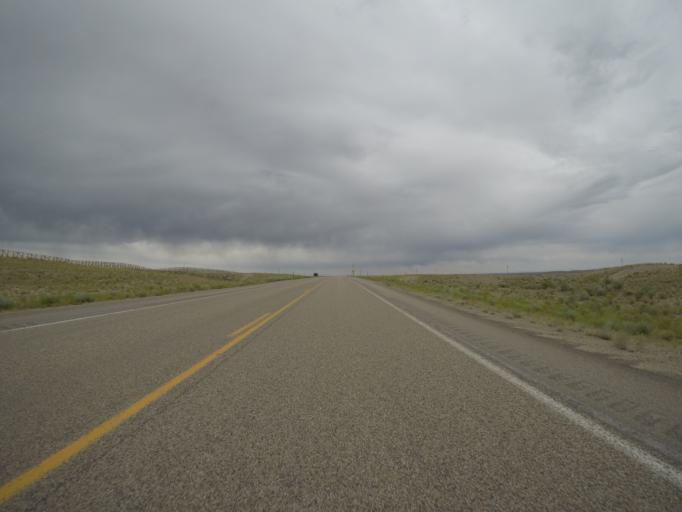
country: US
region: Wyoming
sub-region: Lincoln County
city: Kemmerer
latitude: 41.9764
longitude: -110.0617
